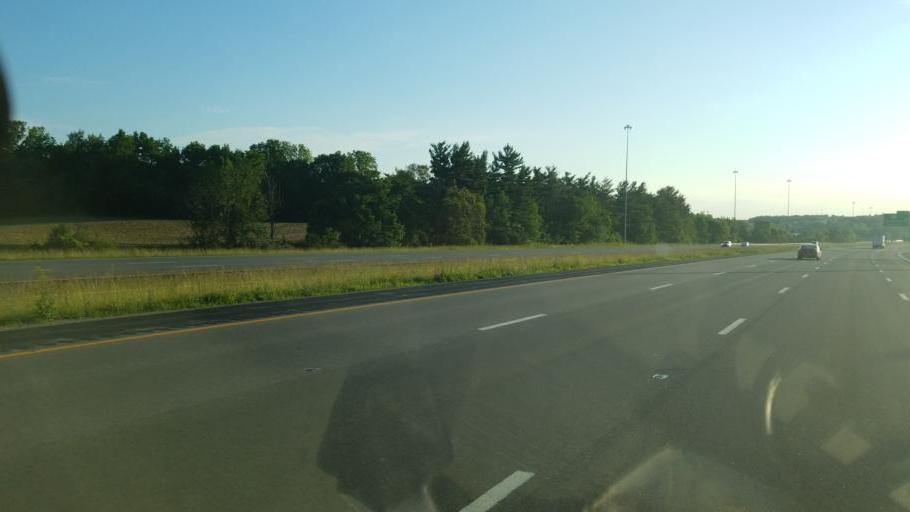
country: US
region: Ohio
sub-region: Richland County
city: Lexington
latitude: 40.6892
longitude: -82.5196
